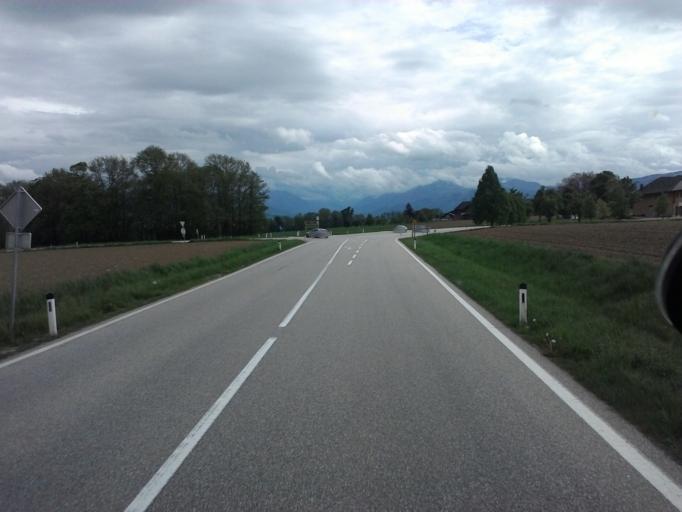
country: AT
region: Upper Austria
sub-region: Politischer Bezirk Kirchdorf an der Krems
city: Kremsmunster
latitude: 47.9826
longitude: 14.0796
